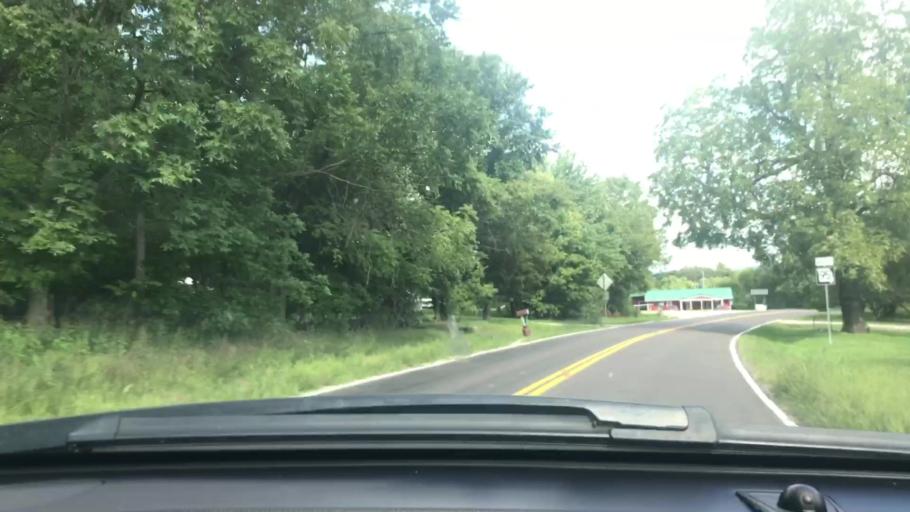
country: US
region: Missouri
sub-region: Wright County
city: Hartville
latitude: 37.3797
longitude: -92.3626
